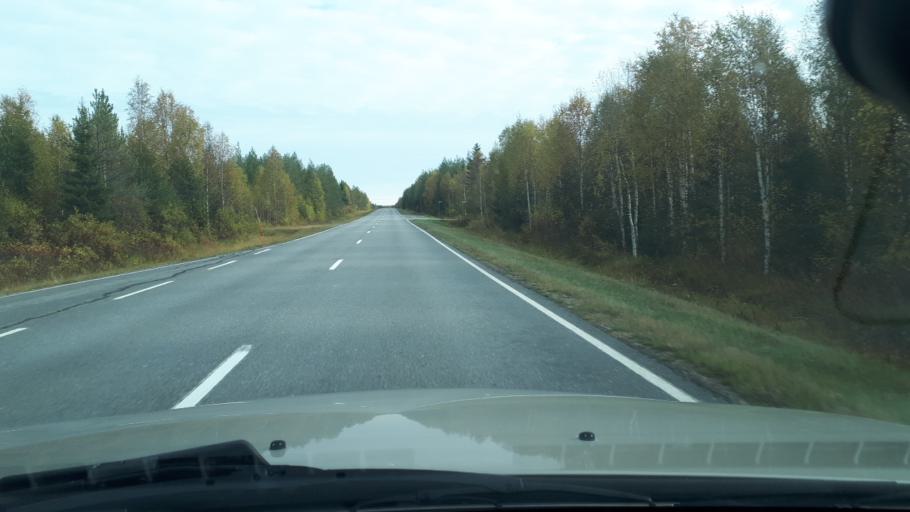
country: FI
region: Lapland
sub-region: Rovaniemi
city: Ranua
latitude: 65.9786
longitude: 26.1274
